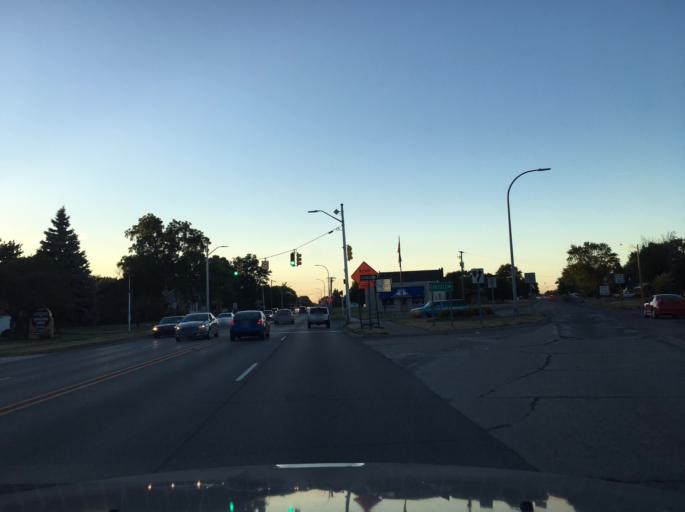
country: US
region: Michigan
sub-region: Macomb County
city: Fraser
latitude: 42.5332
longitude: -82.9494
